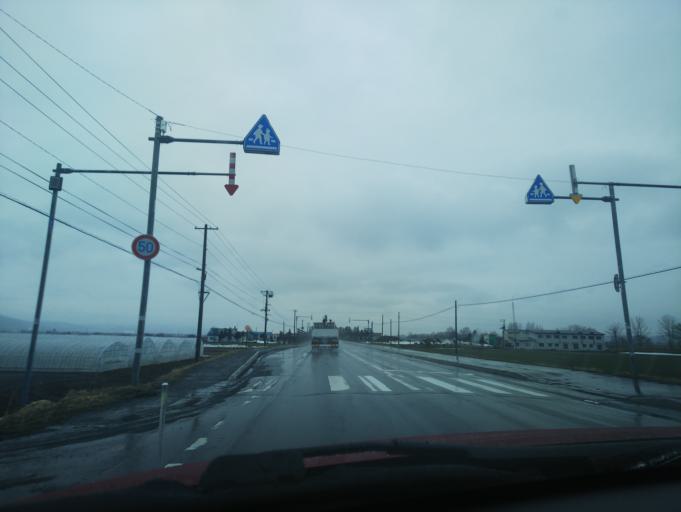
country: JP
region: Hokkaido
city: Nayoro
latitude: 44.2058
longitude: 142.3949
